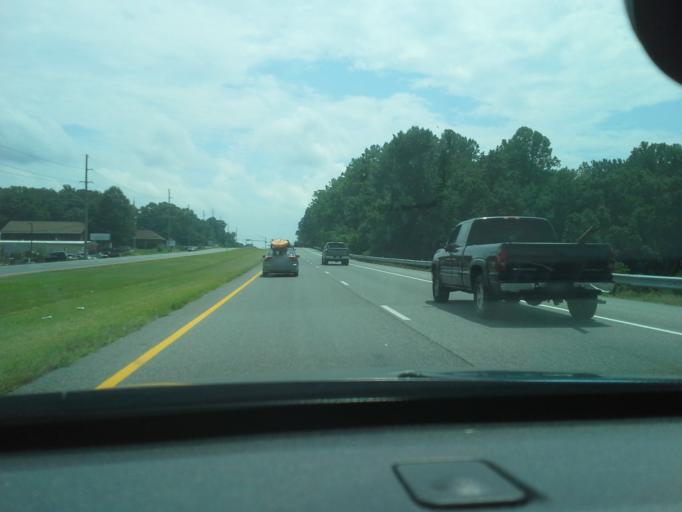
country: US
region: Maryland
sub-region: Calvert County
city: Dunkirk Town Center
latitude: 38.6837
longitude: -76.6347
